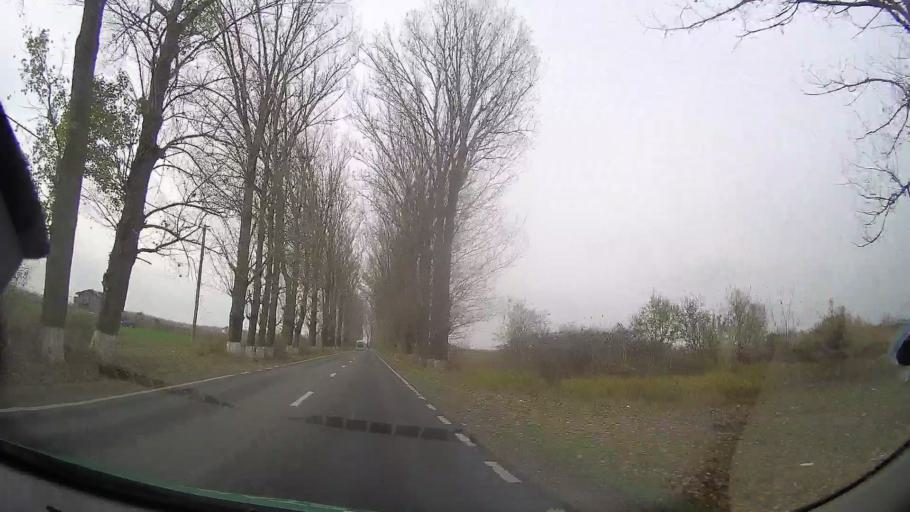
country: RO
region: Ilfov
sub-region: Comuna Gruiu
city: Silistea Snagovului
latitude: 44.7444
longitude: 26.2028
